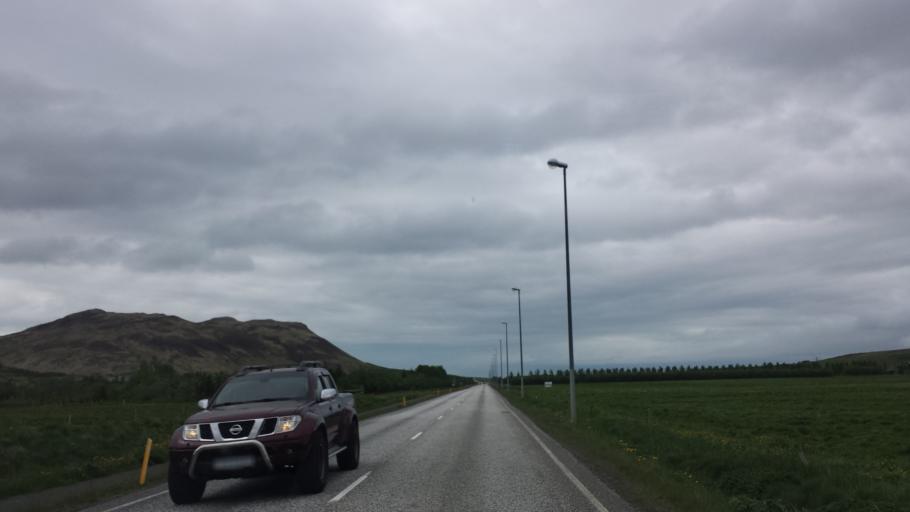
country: IS
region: Capital Region
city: Mosfellsbaer
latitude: 64.1807
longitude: -21.6092
